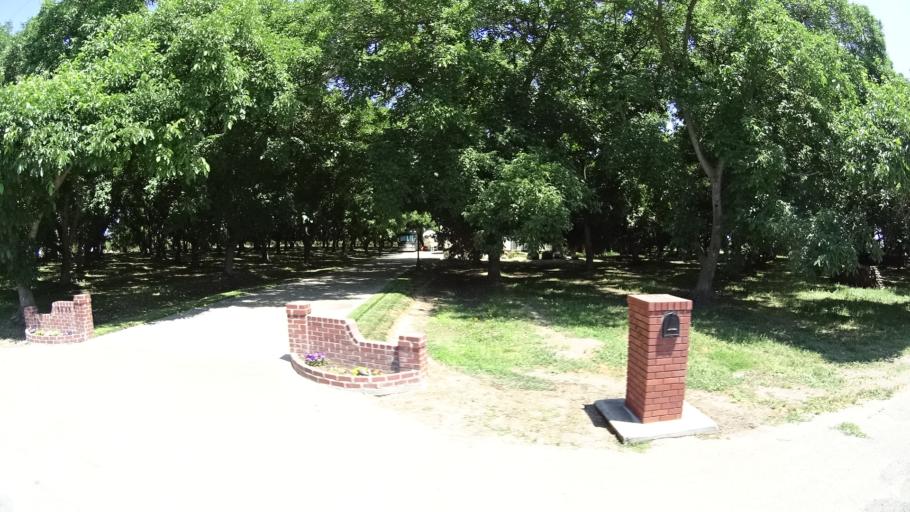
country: US
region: California
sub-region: Kings County
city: Lucerne
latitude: 36.3911
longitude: -119.6550
